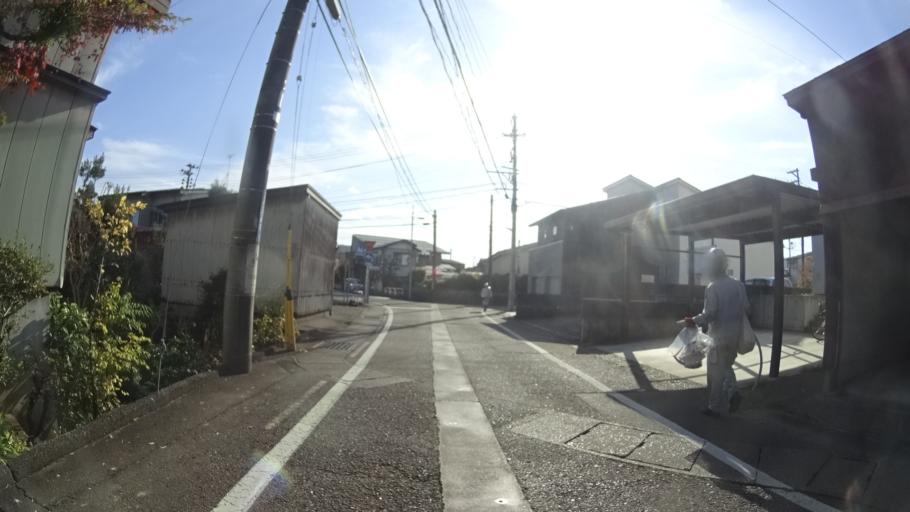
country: JP
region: Niigata
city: Joetsu
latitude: 37.1059
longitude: 138.2450
